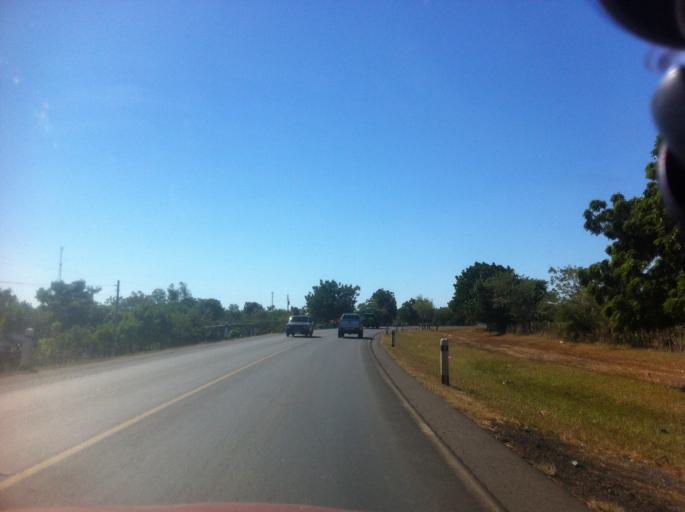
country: NI
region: Managua
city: Tipitapa
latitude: 12.3102
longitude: -86.0435
